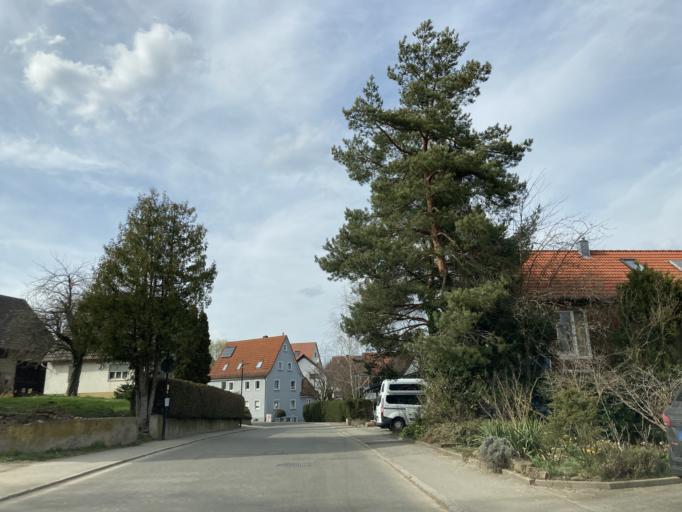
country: DE
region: Baden-Wuerttemberg
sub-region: Tuebingen Region
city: Kusterdingen
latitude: 48.5207
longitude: 9.1184
